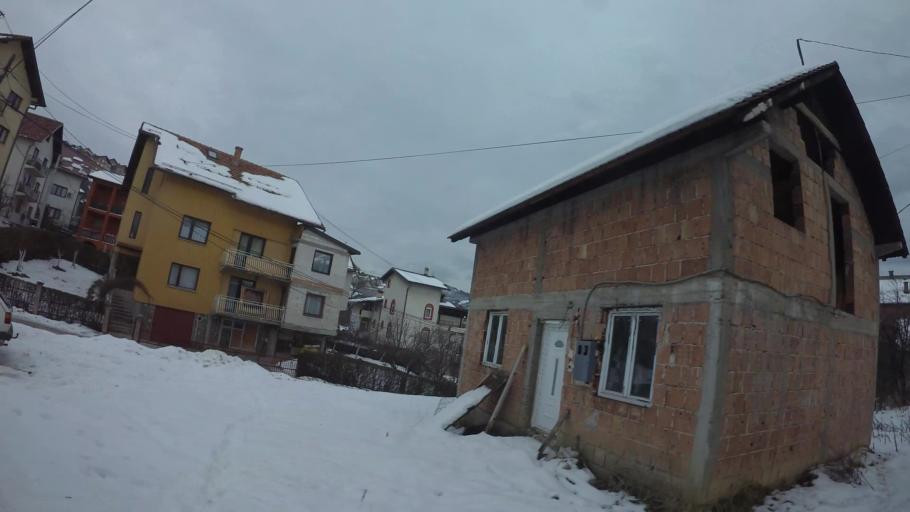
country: BA
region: Federation of Bosnia and Herzegovina
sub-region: Kanton Sarajevo
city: Sarajevo
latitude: 43.8609
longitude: 18.3621
